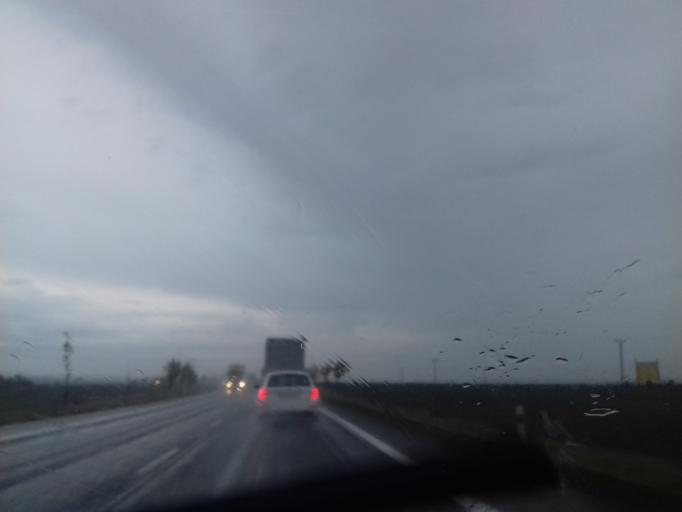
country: CZ
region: Pardubicky
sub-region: Okres Svitavy
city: Litomysl
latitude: 49.8469
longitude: 16.3704
